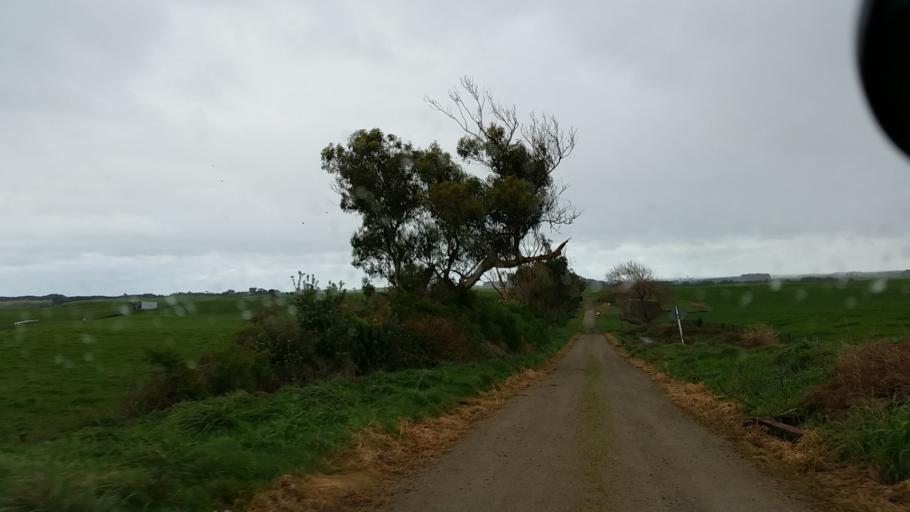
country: NZ
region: Taranaki
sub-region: South Taranaki District
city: Patea
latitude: -39.7689
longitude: 174.6408
